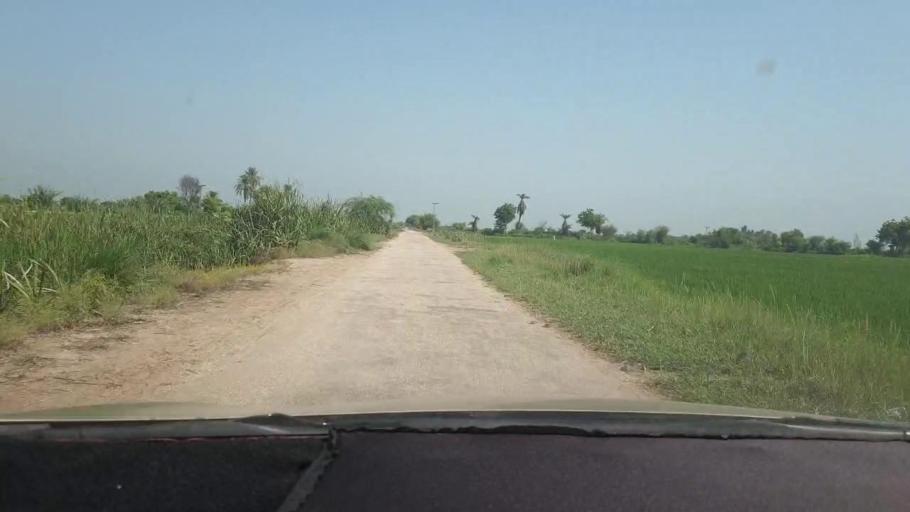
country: PK
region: Sindh
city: Miro Khan
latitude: 27.6944
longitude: 68.1002
